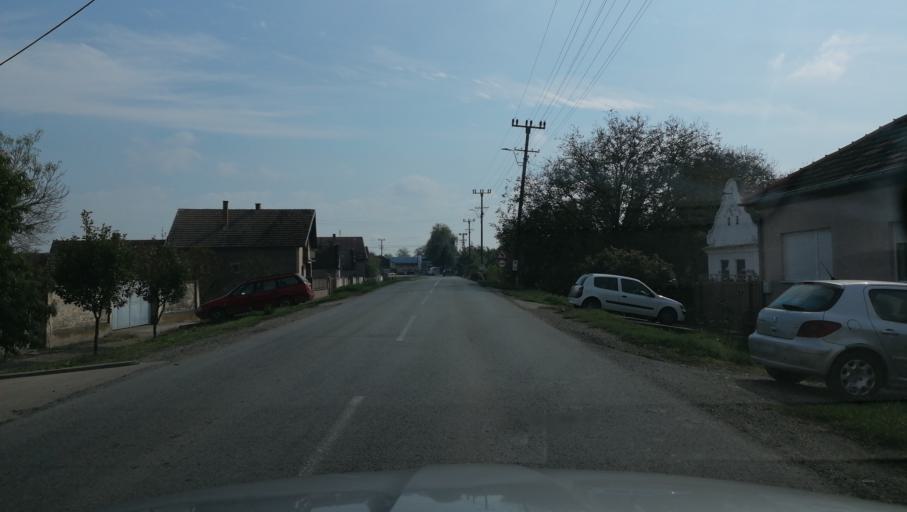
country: RS
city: Ravnje
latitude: 45.0259
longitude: 19.3956
